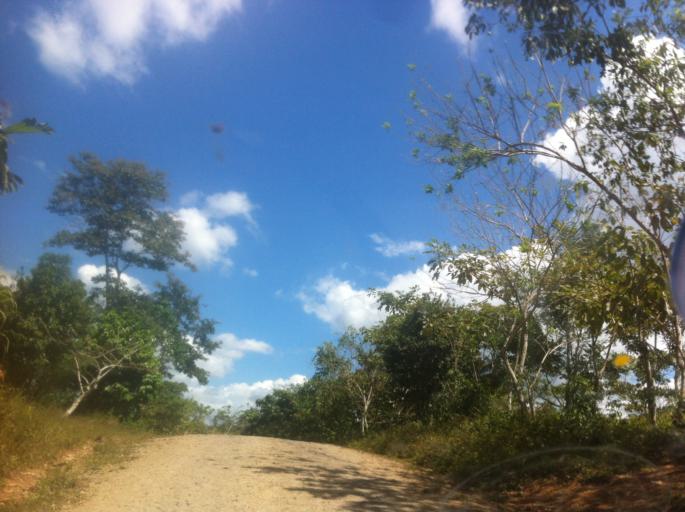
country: CR
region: Alajuela
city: Los Chiles
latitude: 11.2338
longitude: -84.4926
